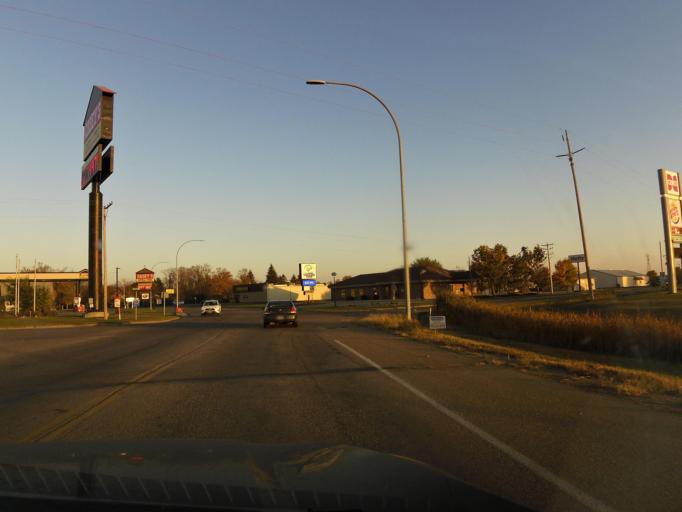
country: US
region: North Dakota
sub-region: Traill County
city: Hillsboro
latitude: 47.4031
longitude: -97.0714
